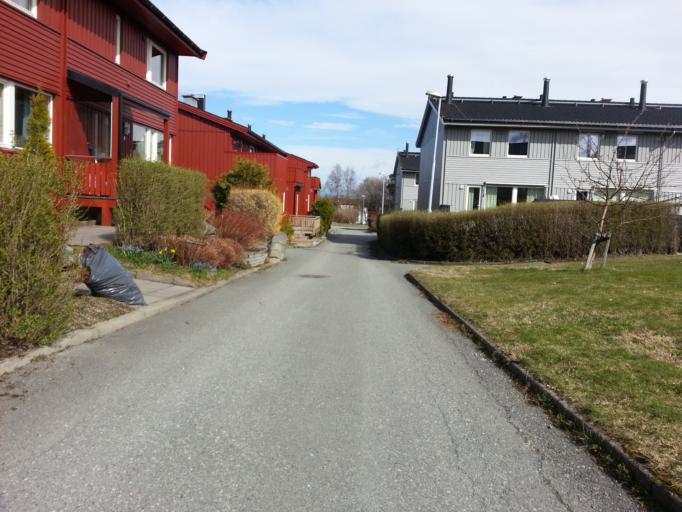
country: NO
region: Sor-Trondelag
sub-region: Trondheim
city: Trondheim
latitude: 63.4276
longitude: 10.4521
